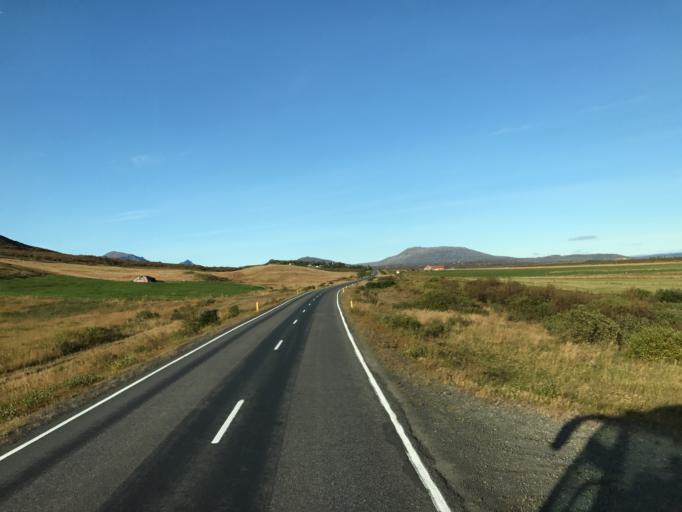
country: IS
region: South
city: Selfoss
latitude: 64.2299
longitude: -20.5673
